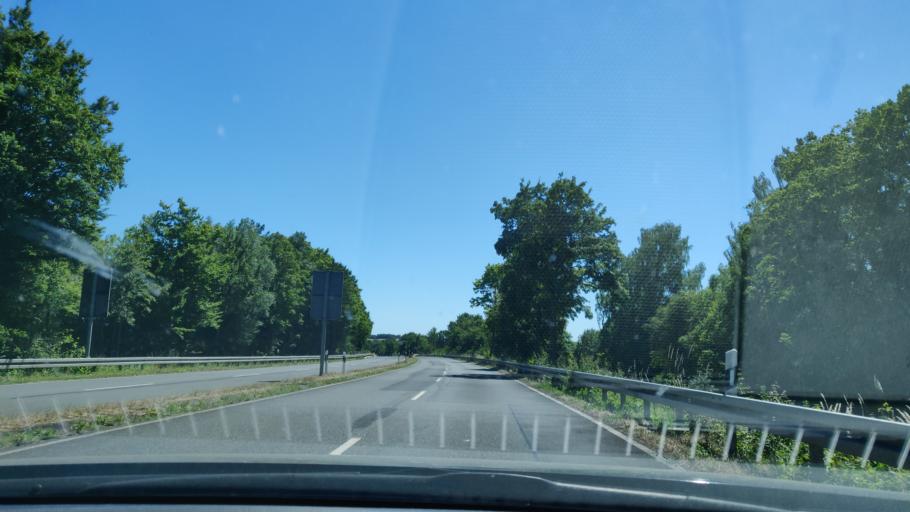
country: DE
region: Hesse
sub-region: Regierungsbezirk Kassel
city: Baunatal
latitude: 51.2596
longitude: 9.4220
